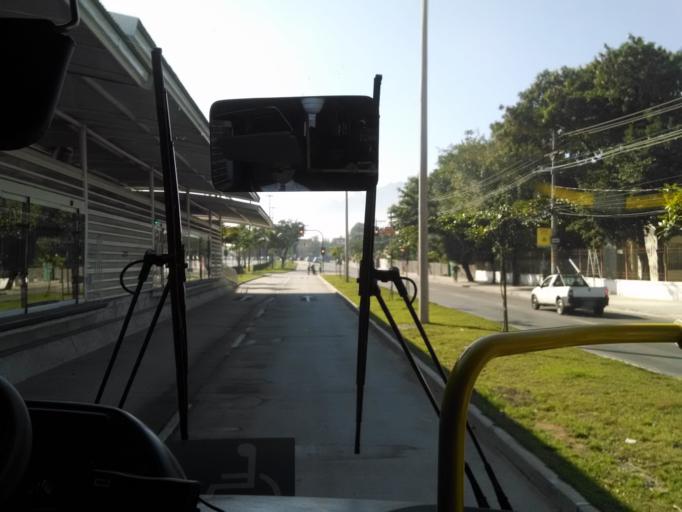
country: BR
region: Rio de Janeiro
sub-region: Nilopolis
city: Nilopolis
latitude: -22.9588
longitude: -43.3835
